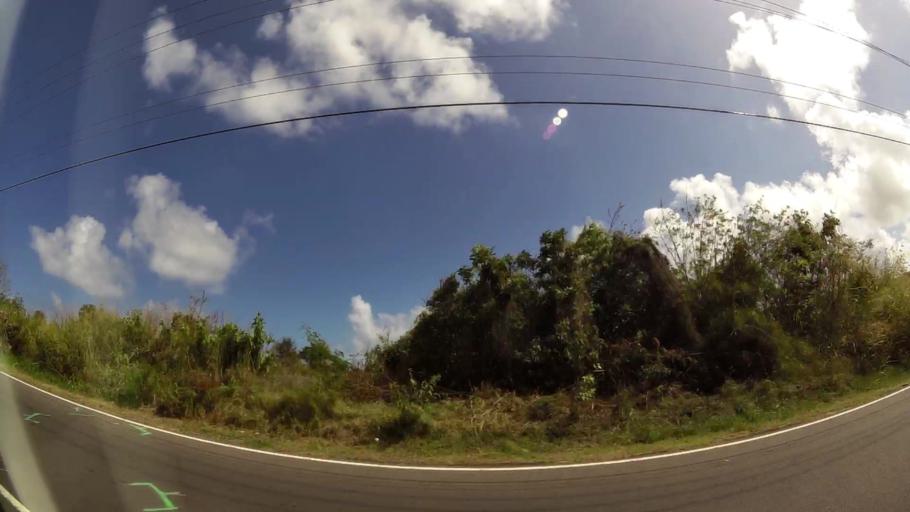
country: LC
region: Micoud Quarter
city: Micoud
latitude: 13.8024
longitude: -60.9037
